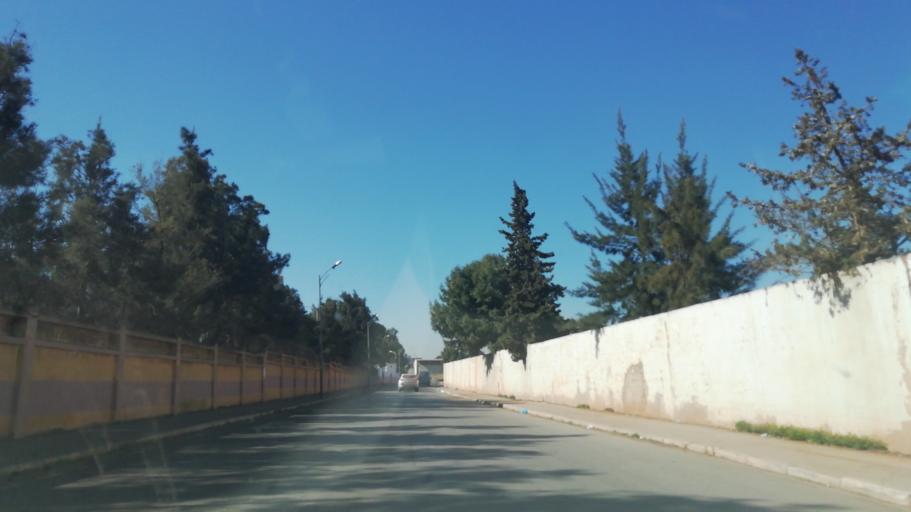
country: DZ
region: Oran
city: Es Senia
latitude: 35.6650
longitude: -0.6274
